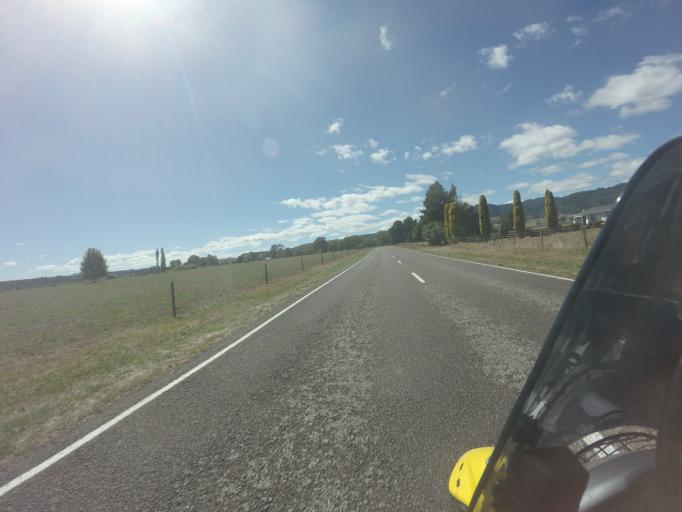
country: NZ
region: Bay of Plenty
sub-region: Whakatane District
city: Murupara
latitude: -38.3415
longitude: 176.7915
